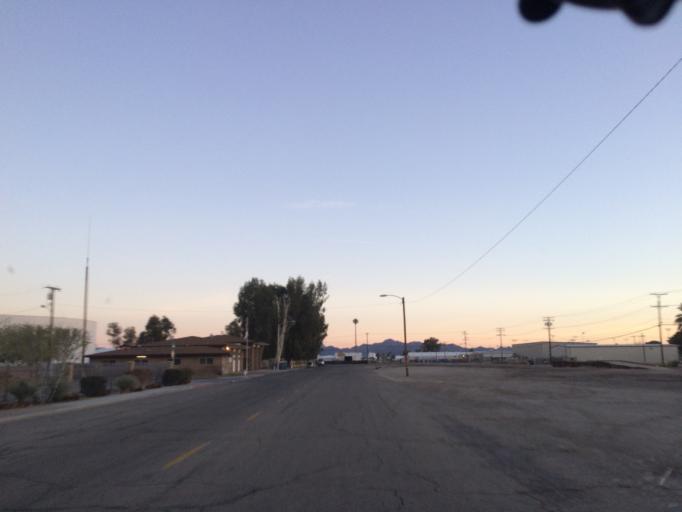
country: US
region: California
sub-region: Riverside County
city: Blythe
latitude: 33.6115
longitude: -114.6009
